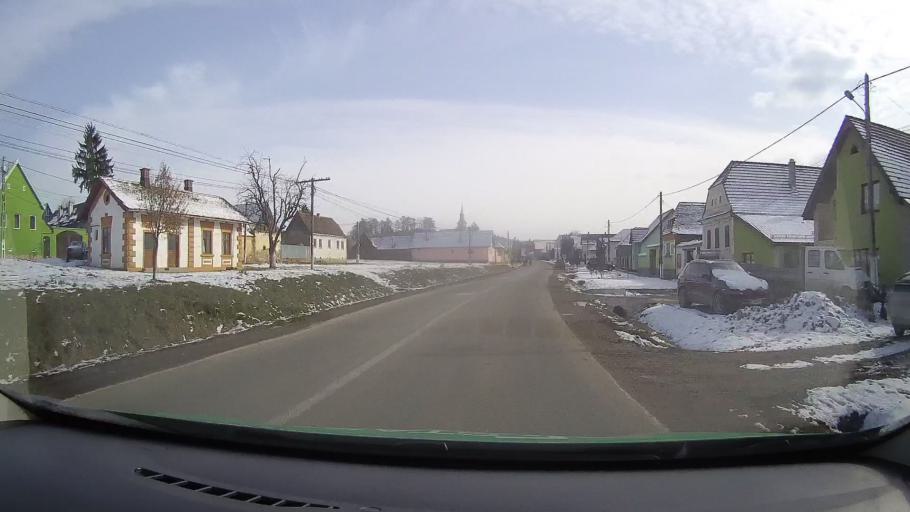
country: RO
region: Mures
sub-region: Comuna Apold
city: Saes
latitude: 46.1586
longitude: 24.7658
